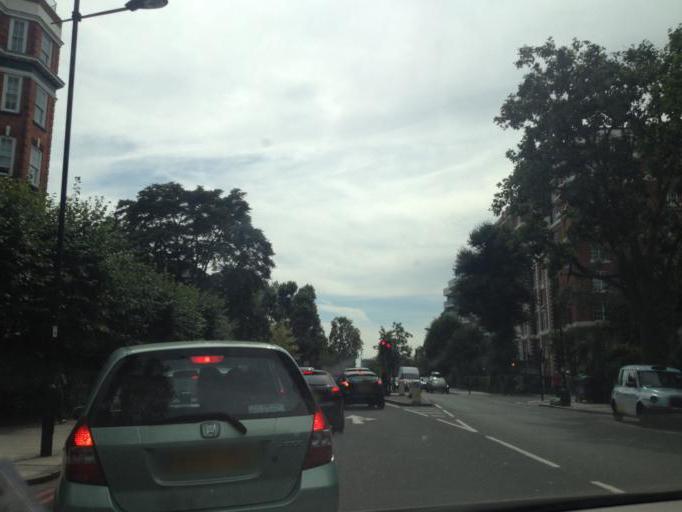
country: GB
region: England
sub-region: Greater London
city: Belsize Park
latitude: 51.5280
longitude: -0.1733
